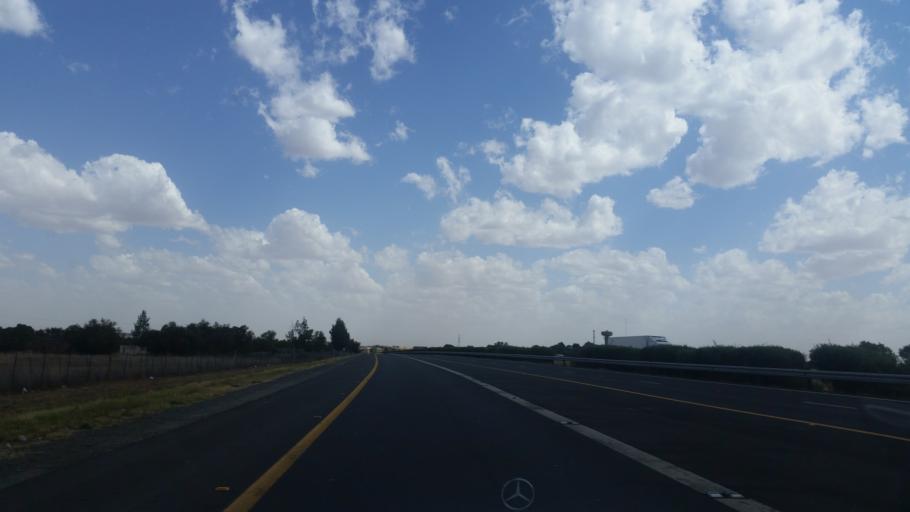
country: ZA
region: Orange Free State
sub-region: Mangaung Metropolitan Municipality
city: Bloemfontein
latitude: -29.0765
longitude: 26.1810
